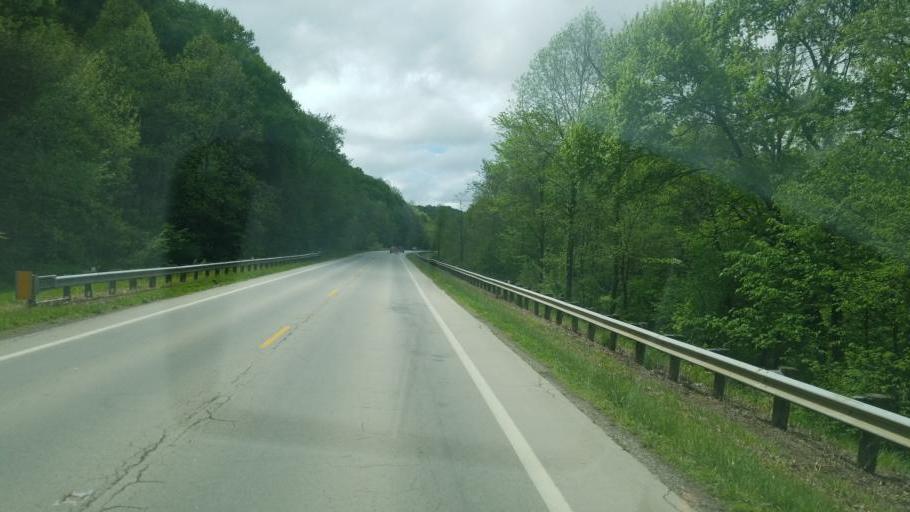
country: US
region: Ohio
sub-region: Tuscarawas County
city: Rockford
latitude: 40.4721
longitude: -81.3439
